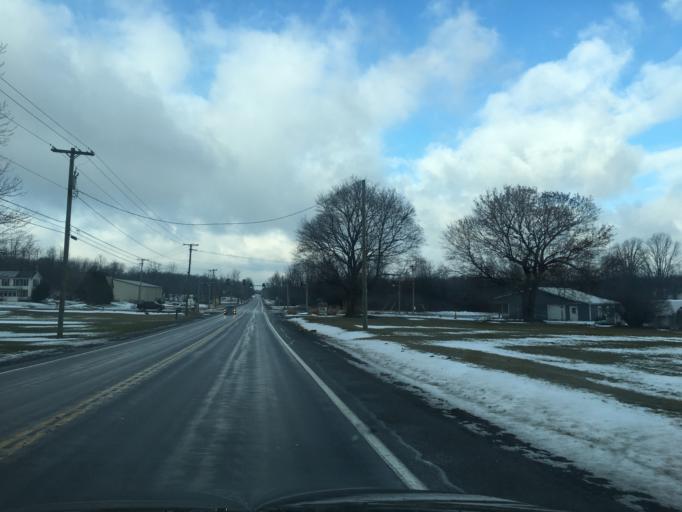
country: US
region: New York
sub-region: Ontario County
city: Manchester
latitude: 42.9670
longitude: -77.2754
